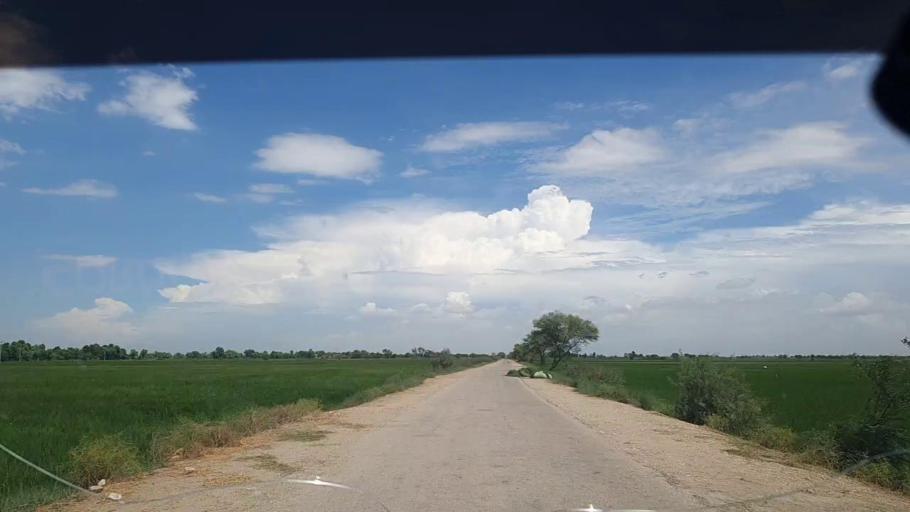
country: PK
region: Sindh
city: Ghauspur
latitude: 28.1557
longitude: 69.0054
